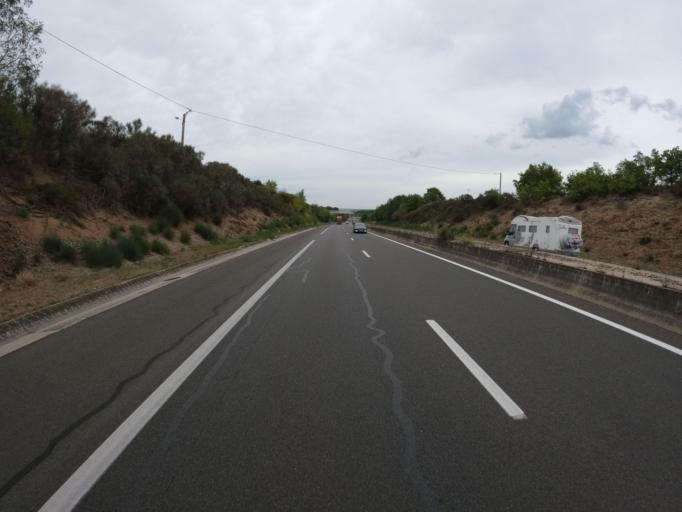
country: FR
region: Auvergne
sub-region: Departement de l'Allier
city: Domerat
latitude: 46.3446
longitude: 2.5395
